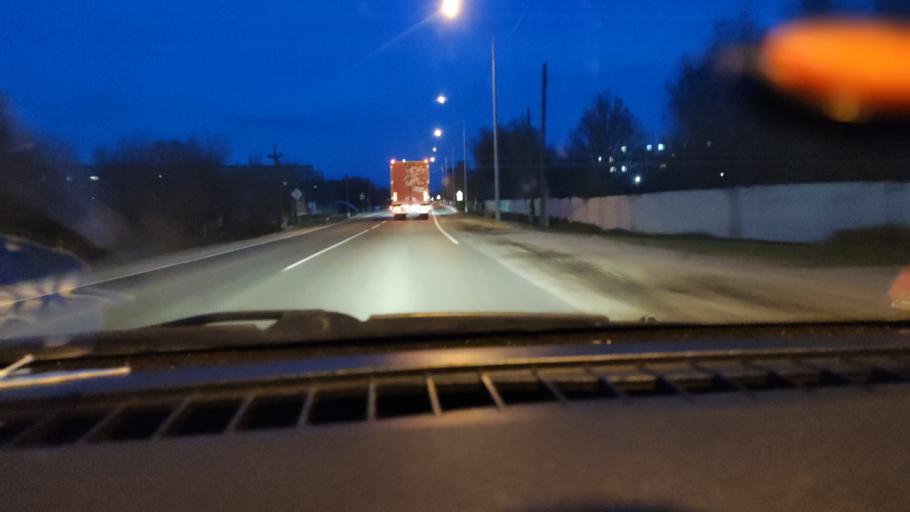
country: RU
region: Saratov
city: Sennoy
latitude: 52.1522
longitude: 46.9593
